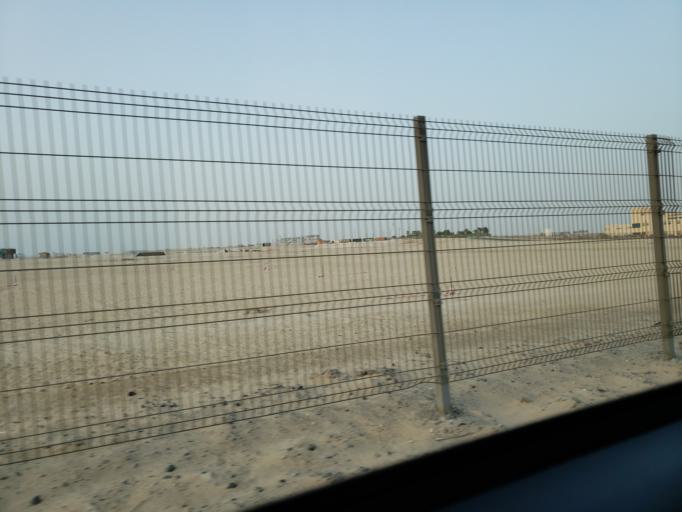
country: AE
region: Ajman
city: Ajman
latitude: 25.4290
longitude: 55.4561
